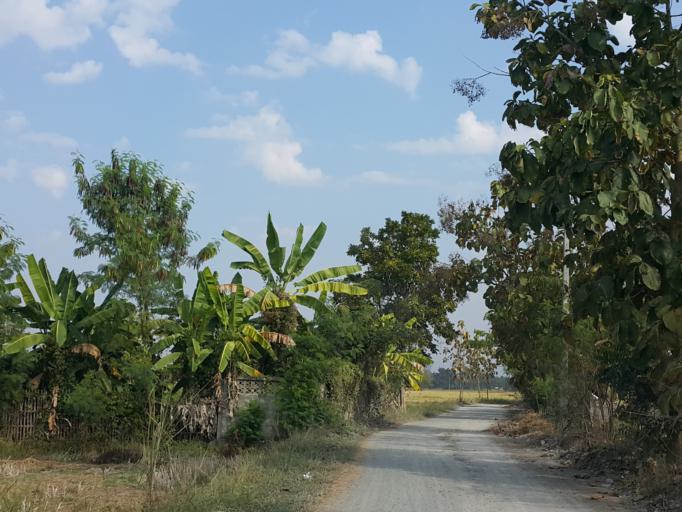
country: TH
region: Chiang Mai
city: San Sai
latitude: 18.8348
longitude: 99.1186
